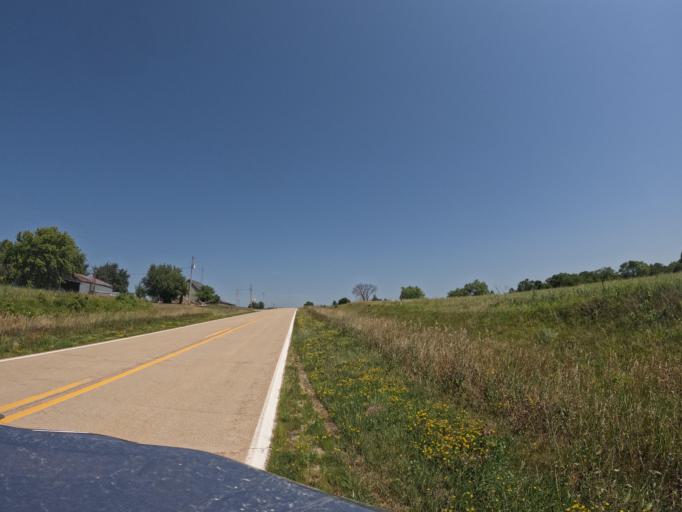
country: US
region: Iowa
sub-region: Henry County
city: Mount Pleasant
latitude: 40.8667
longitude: -91.5599
